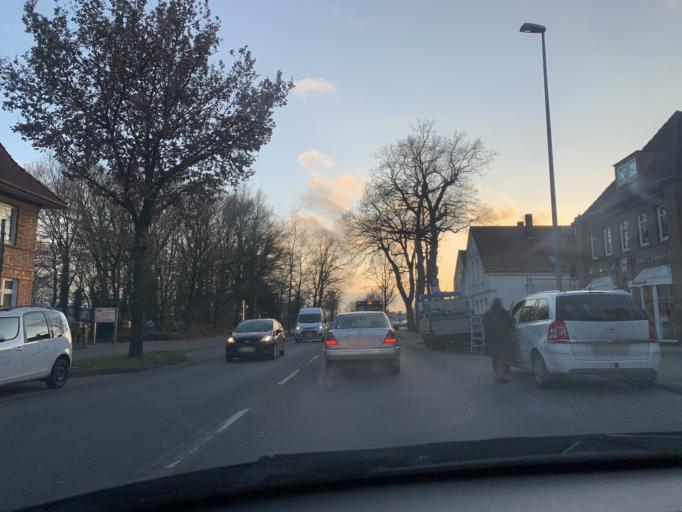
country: DE
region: Lower Saxony
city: Oldenburg
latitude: 53.1686
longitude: 8.2286
